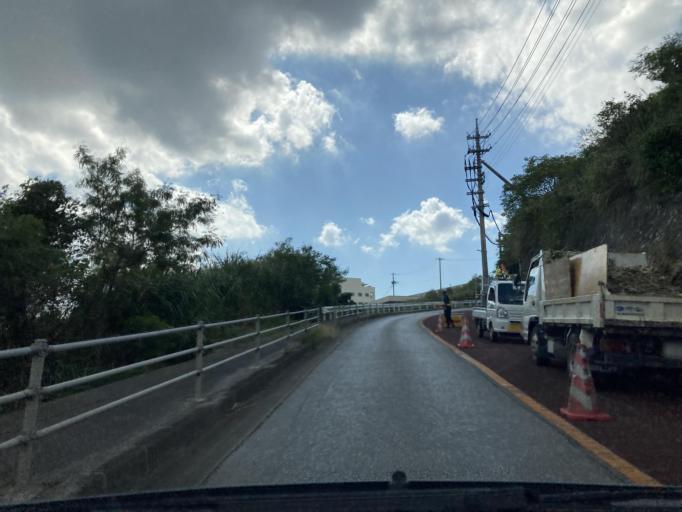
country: JP
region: Okinawa
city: Ginowan
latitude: 26.2500
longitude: 127.7760
